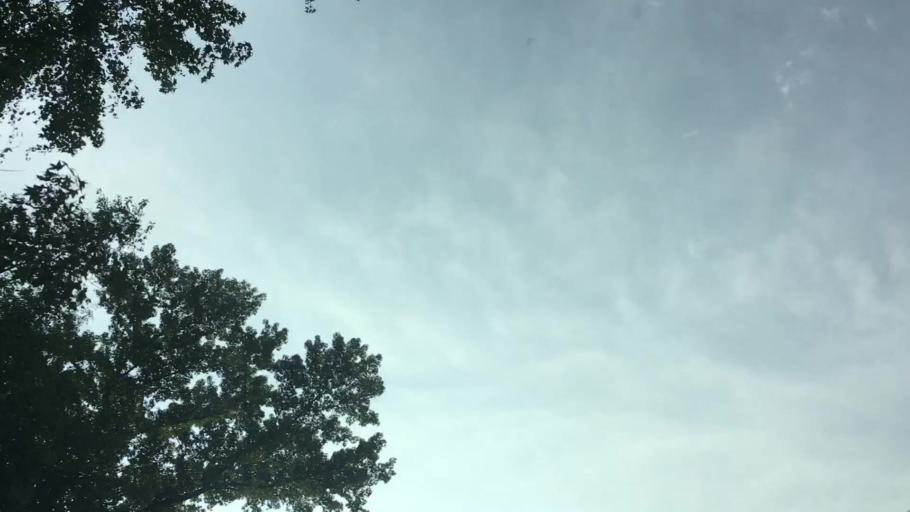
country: US
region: Alabama
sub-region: Bibb County
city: Woodstock
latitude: 33.2183
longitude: -87.1107
